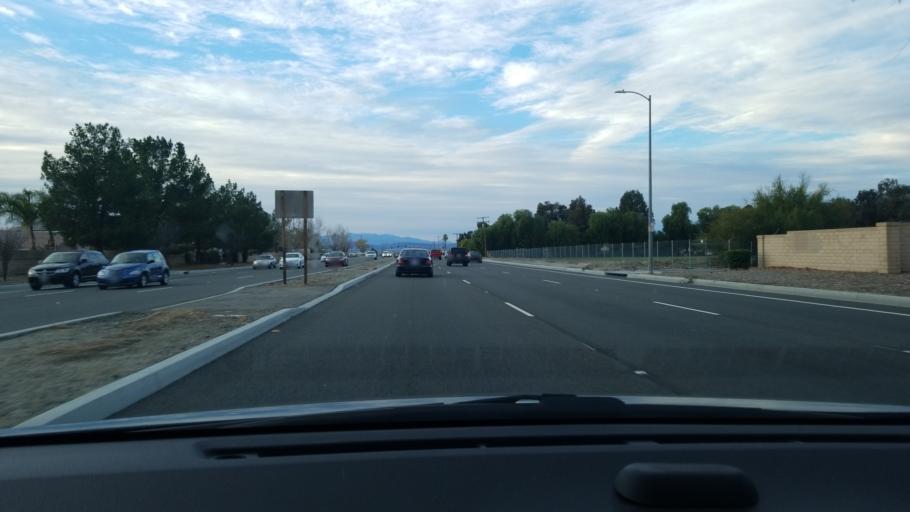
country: US
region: California
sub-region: Riverside County
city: San Jacinto
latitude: 33.8075
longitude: -116.9810
